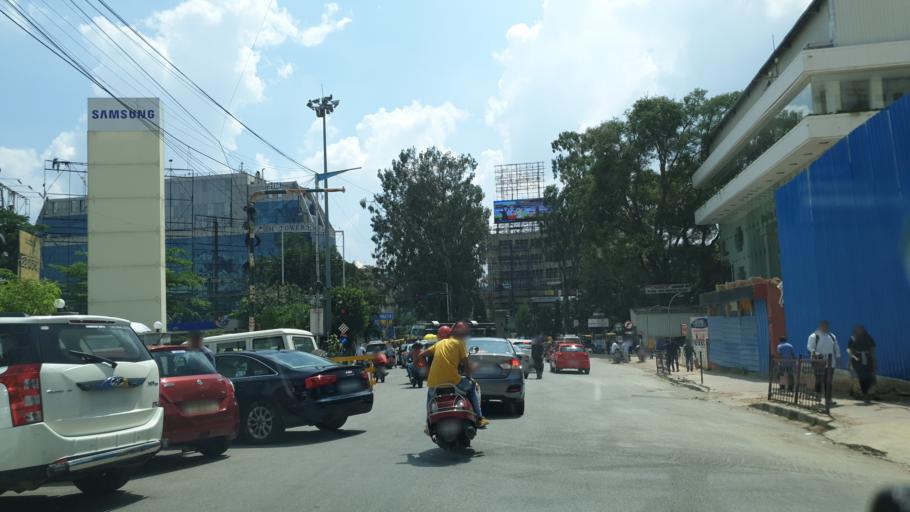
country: IN
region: Karnataka
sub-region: Bangalore Urban
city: Bangalore
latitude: 12.9726
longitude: 77.6071
